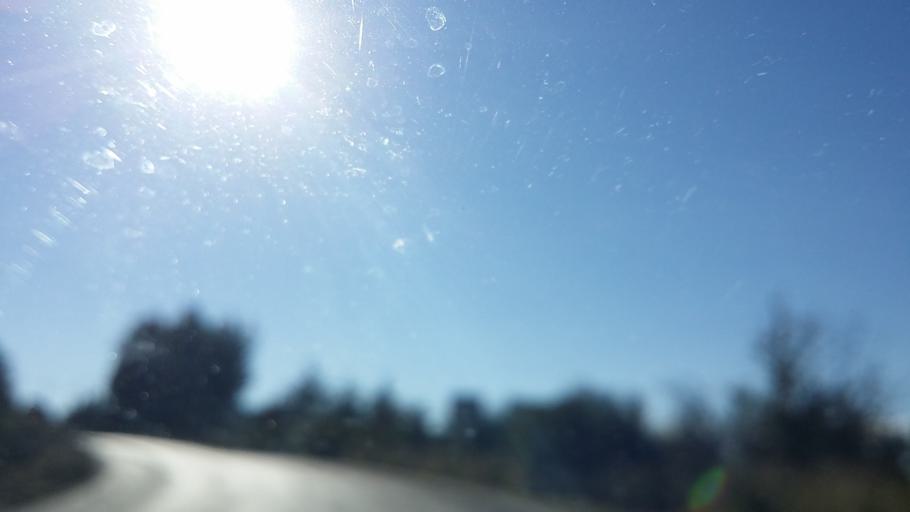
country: GR
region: West Greece
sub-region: Nomos Aitolias kai Akarnanias
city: Palairos
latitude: 38.7653
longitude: 20.8817
